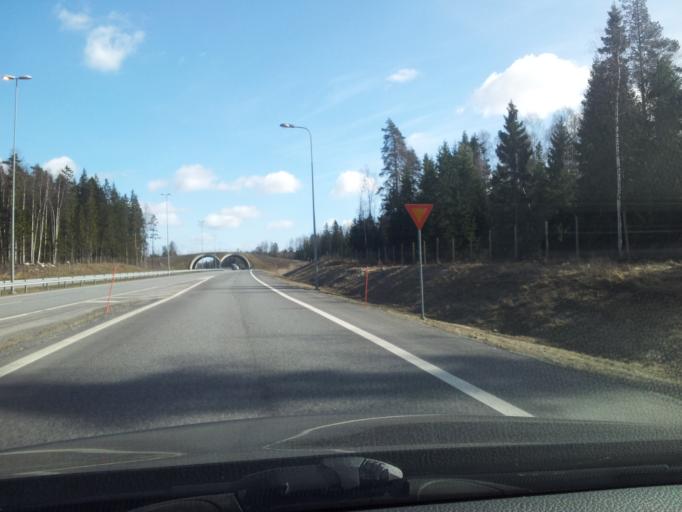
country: FI
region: Uusimaa
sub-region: Helsinki
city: Kirkkonummi
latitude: 60.1385
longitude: 24.5408
